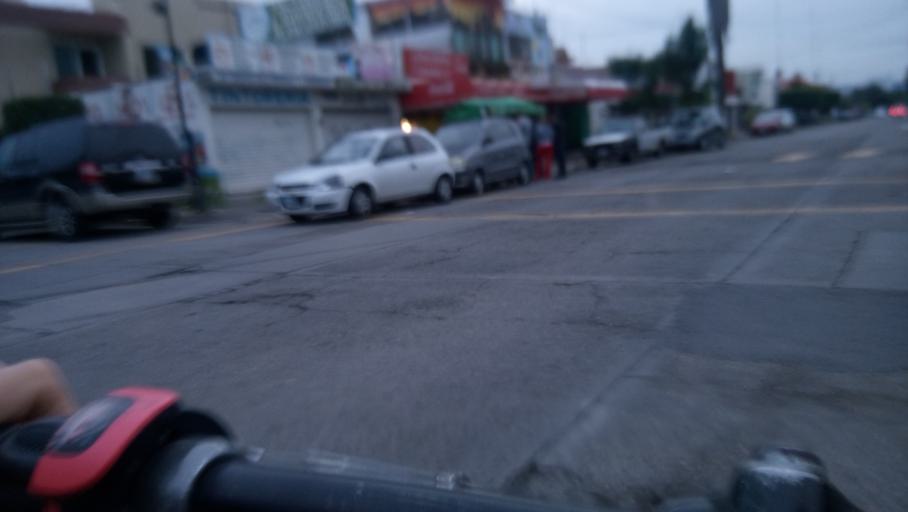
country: MX
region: Guanajuato
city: Leon
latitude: 21.1471
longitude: -101.6680
